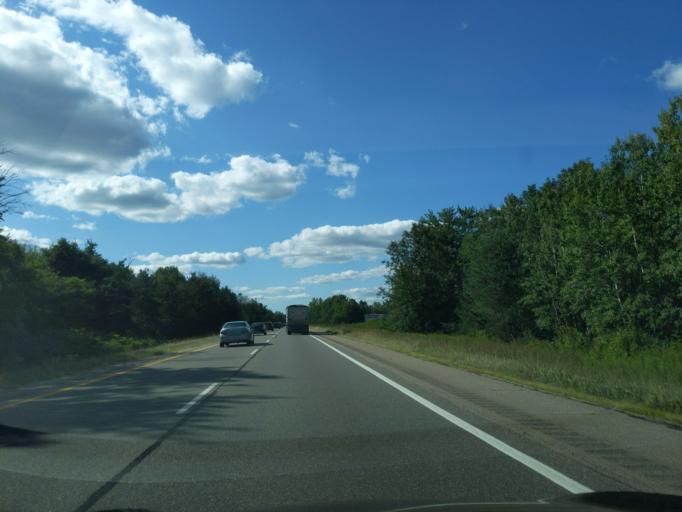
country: US
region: Michigan
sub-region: Muskegon County
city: Fruitport
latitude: 43.0987
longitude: -86.1061
